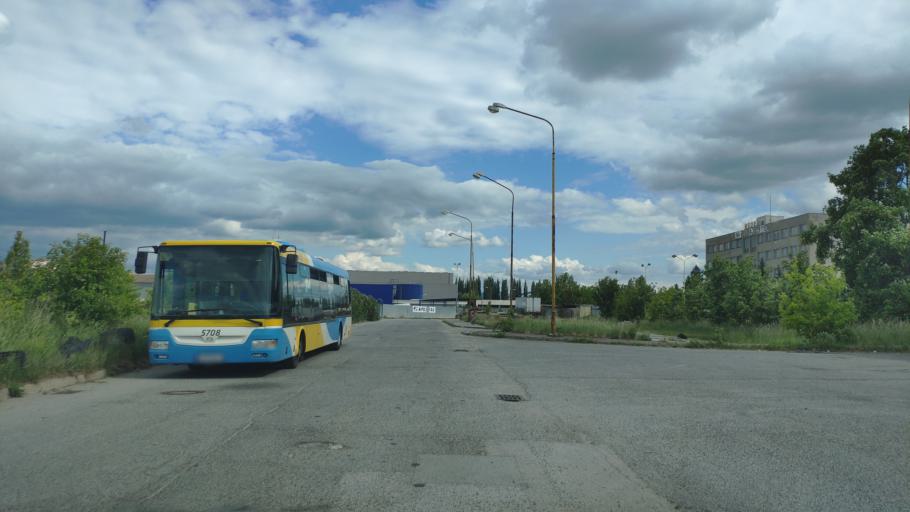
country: SK
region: Kosicky
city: Kosice
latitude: 48.6815
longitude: 21.2864
